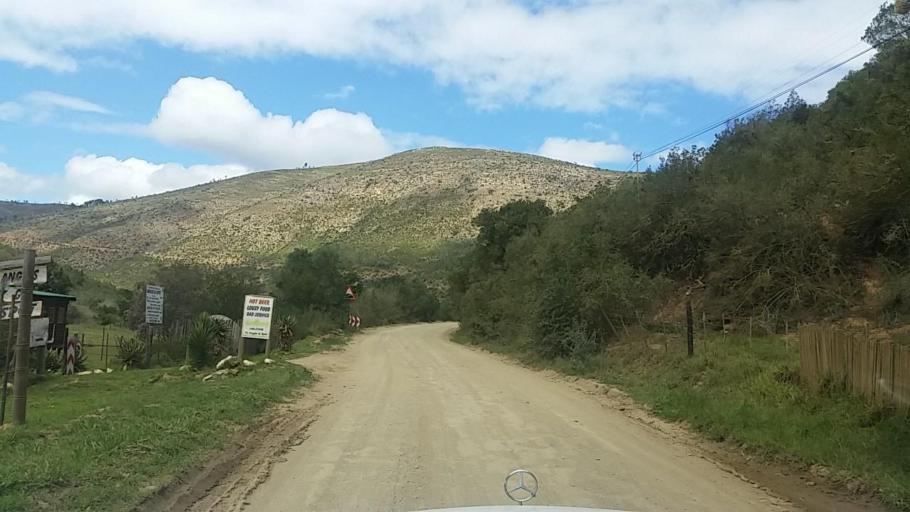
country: ZA
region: Western Cape
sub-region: Eden District Municipality
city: Knysna
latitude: -33.8133
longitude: 23.1749
